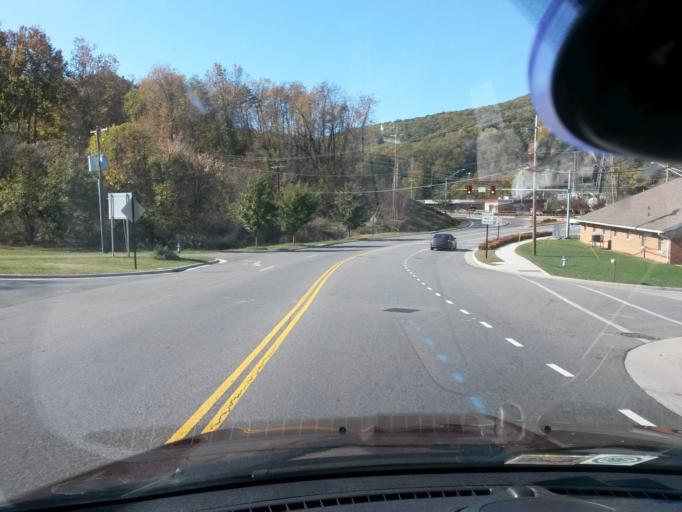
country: US
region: Virginia
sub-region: City of Roanoke
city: Cedar Bluff
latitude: 37.2505
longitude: -79.9159
